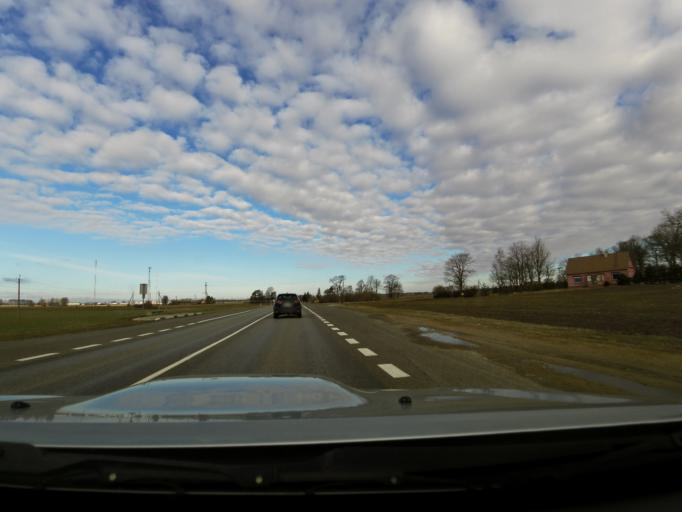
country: LT
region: Siauliu apskritis
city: Pakruojis
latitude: 55.7875
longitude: 24.0359
